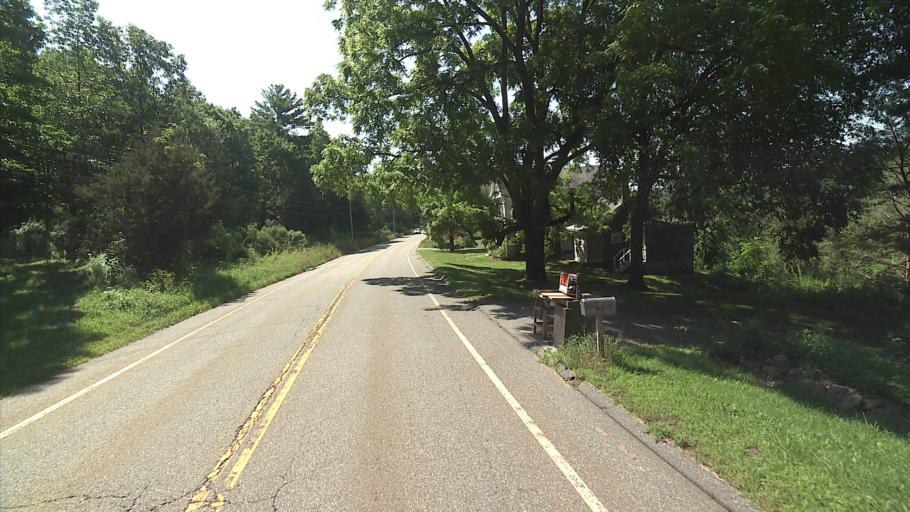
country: US
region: Connecticut
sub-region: Litchfield County
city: New Preston
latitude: 41.7761
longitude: -73.3537
